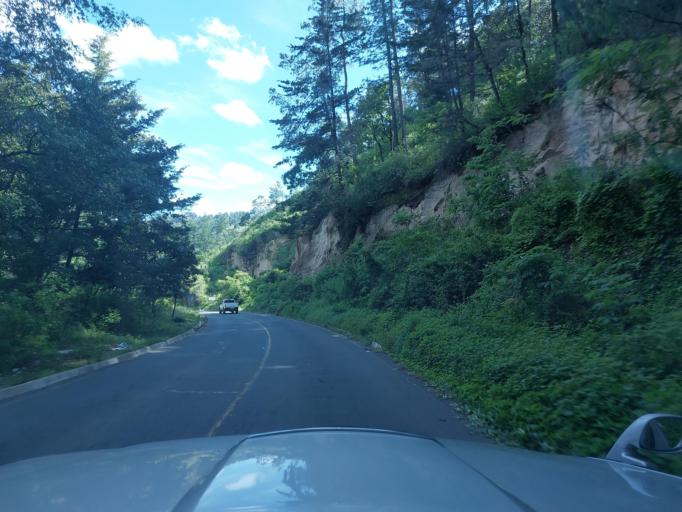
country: GT
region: Chimaltenango
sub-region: Municipio de Santa Cruz Balanya
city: Santa Cruz Balanya
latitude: 14.6891
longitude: -90.8967
